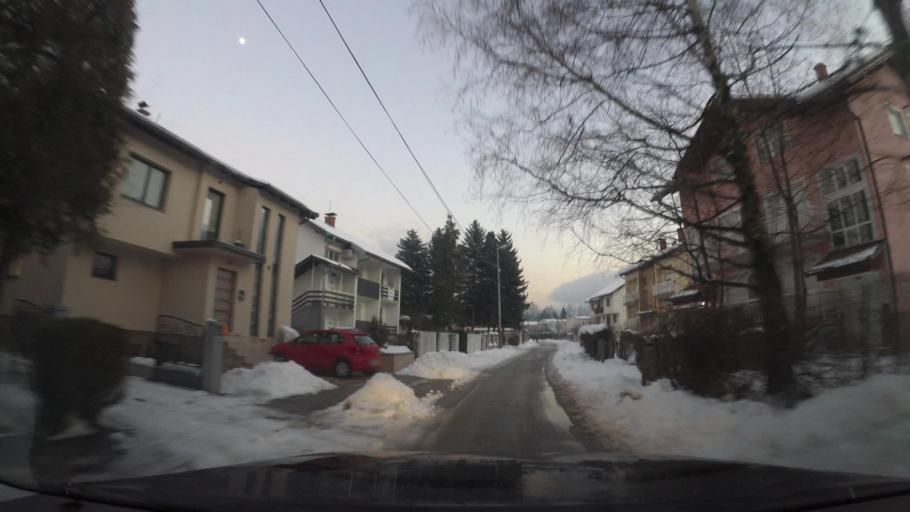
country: BA
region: Federation of Bosnia and Herzegovina
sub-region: Kanton Sarajevo
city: Sarajevo
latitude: 43.8274
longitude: 18.2996
